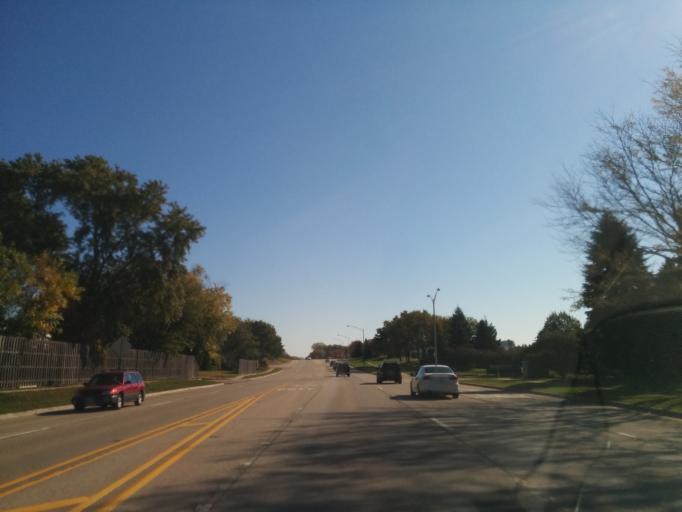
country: US
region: Illinois
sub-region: DuPage County
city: Carol Stream
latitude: 41.9518
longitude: -88.1484
